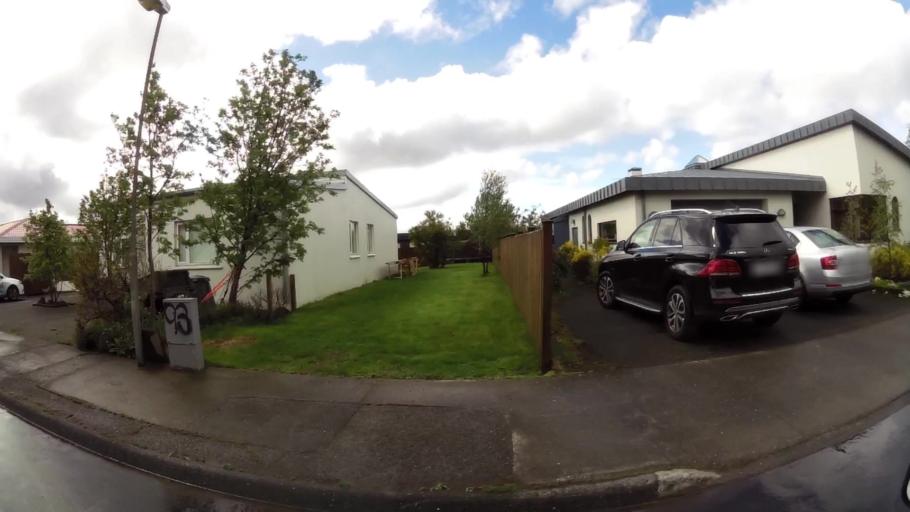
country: IS
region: Capital Region
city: Kopavogur
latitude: 64.1274
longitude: -21.9491
